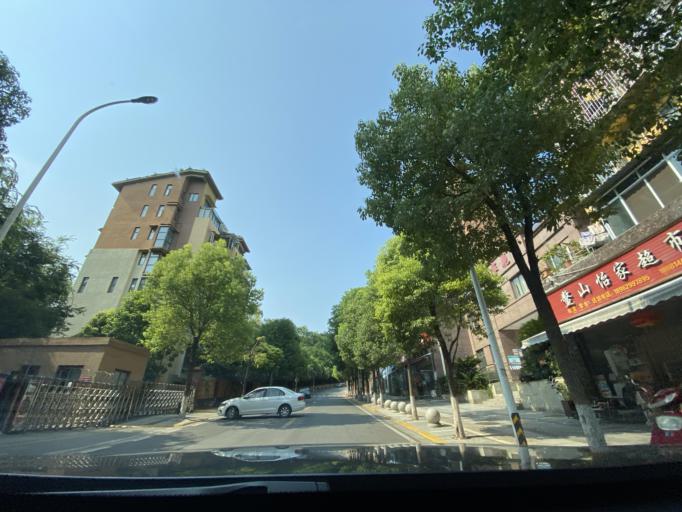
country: CN
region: Sichuan
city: Jiancheng
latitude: 30.4179
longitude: 104.5441
